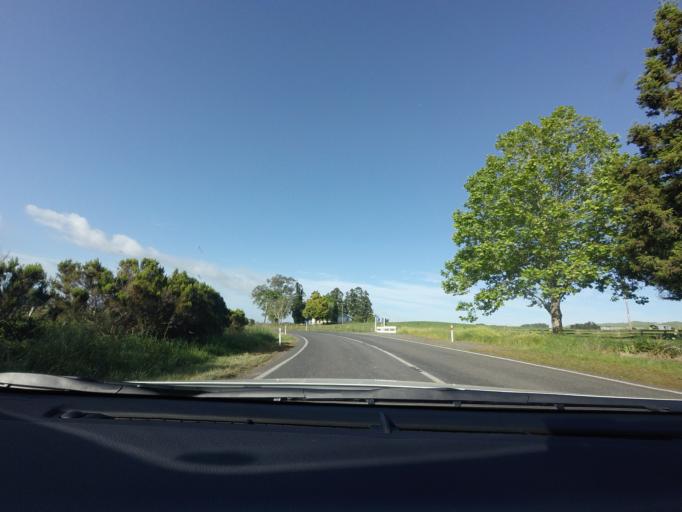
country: NZ
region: Waikato
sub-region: Hauraki District
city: Paeroa
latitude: -37.4729
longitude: 175.5097
